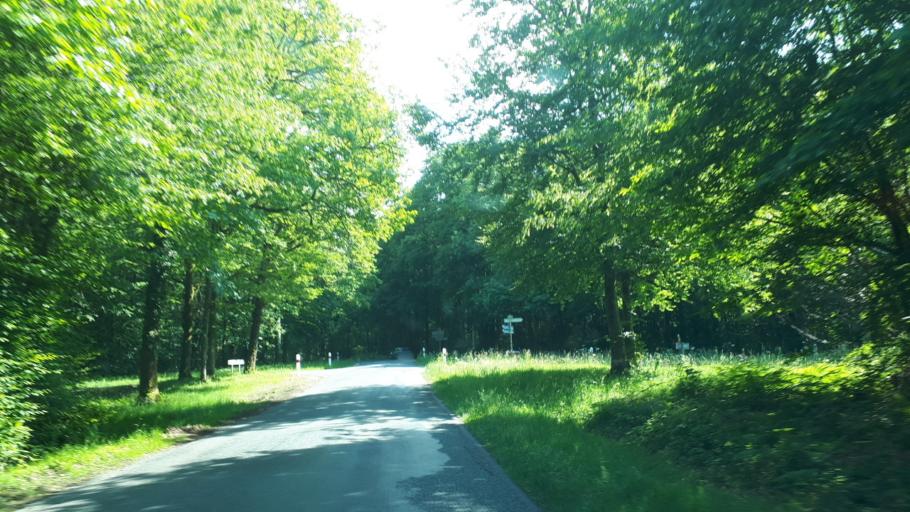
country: FR
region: Centre
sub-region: Departement du Cher
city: Henrichemont
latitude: 47.3961
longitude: 2.5941
